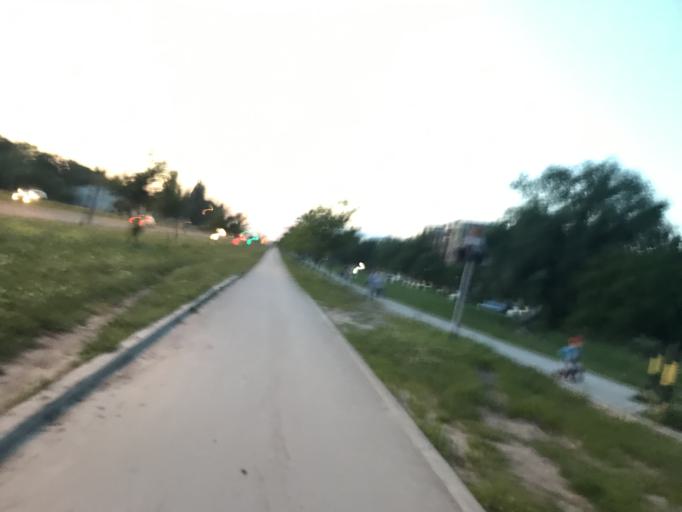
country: RS
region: Autonomna Pokrajina Vojvodina
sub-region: Juznobacki Okrug
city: Novi Sad
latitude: 45.2637
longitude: 19.8066
